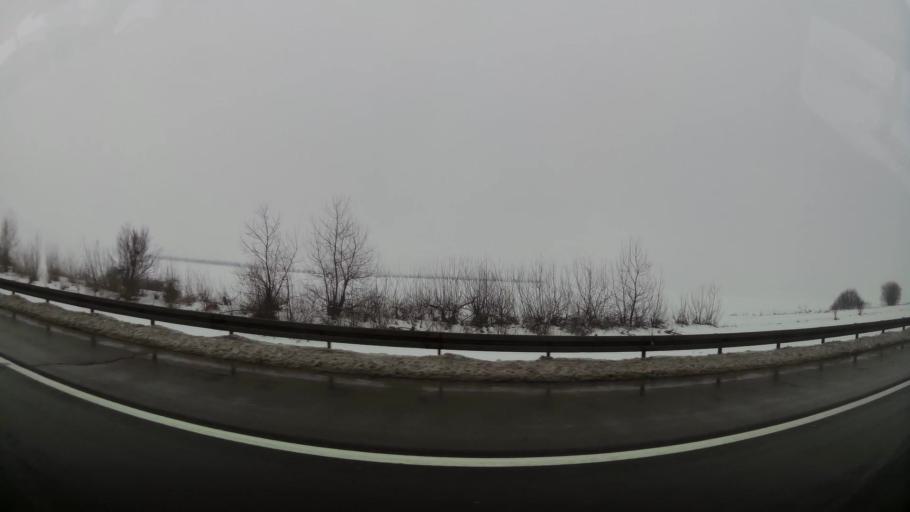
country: RS
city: Dobanovci
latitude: 44.8277
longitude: 20.2518
